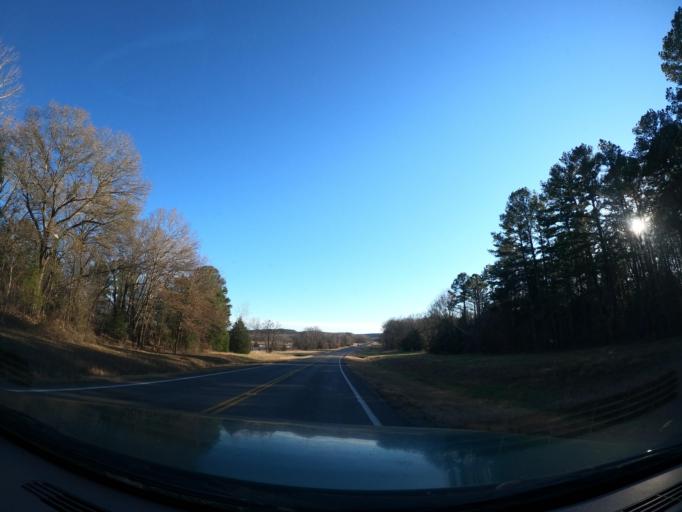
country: US
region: Oklahoma
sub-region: Latimer County
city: Wilburton
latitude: 34.9501
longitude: -95.3416
